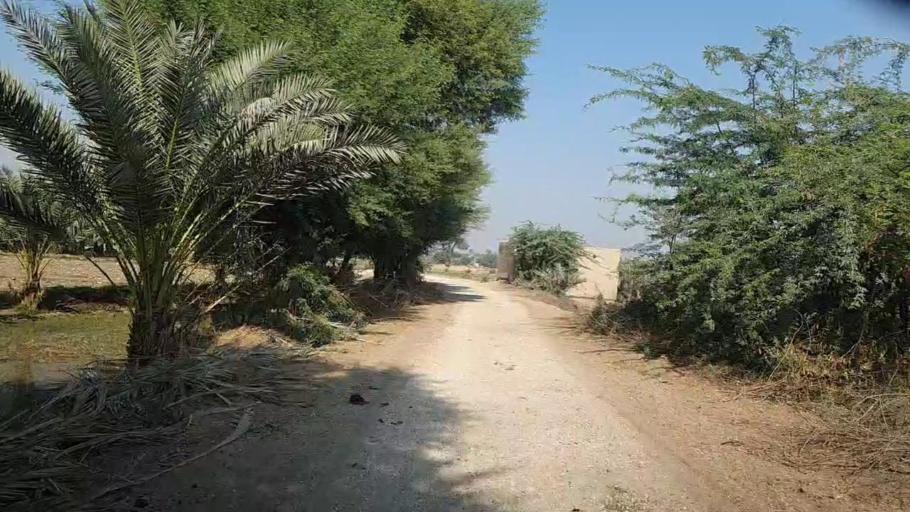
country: PK
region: Sindh
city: Bozdar
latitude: 27.1880
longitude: 68.6119
